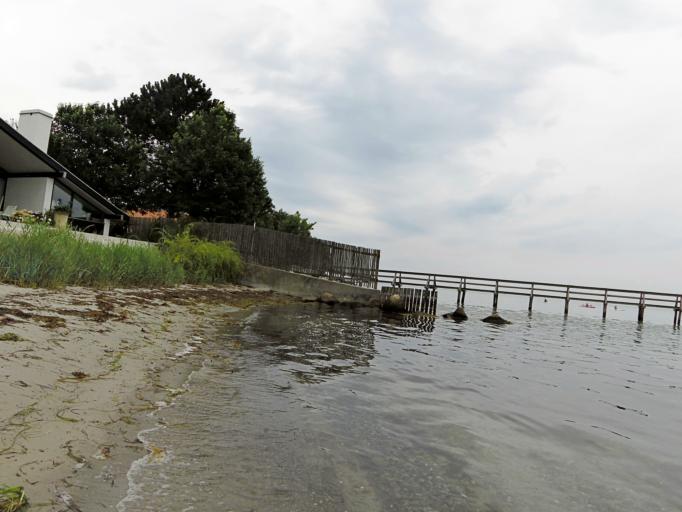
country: DK
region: Capital Region
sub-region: Gentofte Kommune
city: Charlottenlund
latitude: 55.7412
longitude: 12.5858
